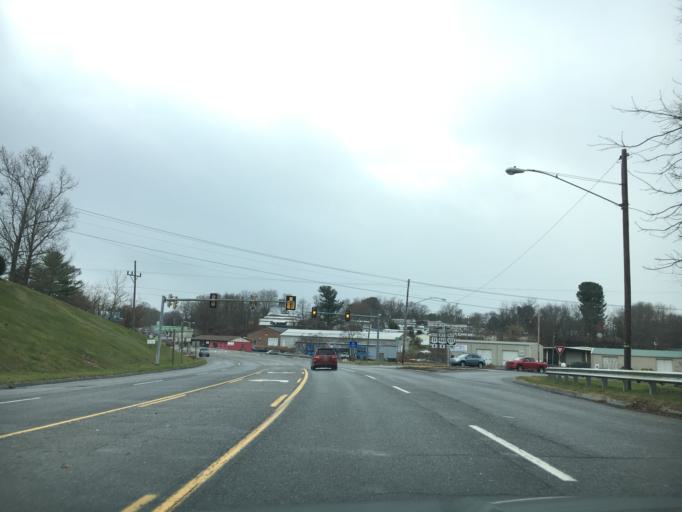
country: US
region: Virginia
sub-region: Montgomery County
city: Christiansburg
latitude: 37.1343
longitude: -80.3887
